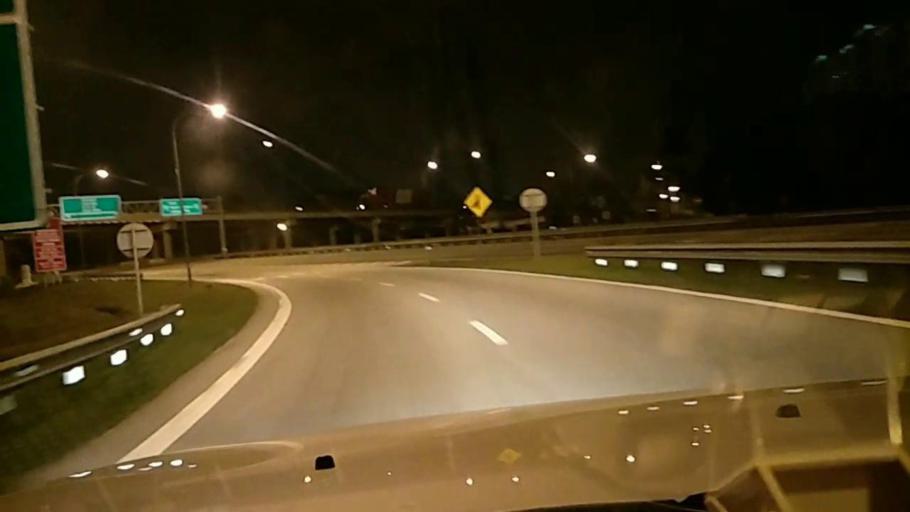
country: MY
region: Selangor
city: Shah Alam
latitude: 3.0932
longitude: 101.5473
